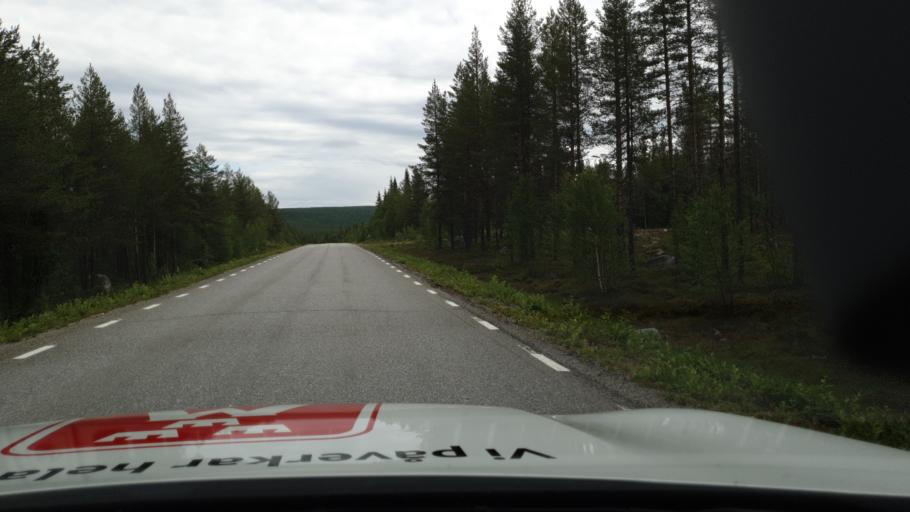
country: SE
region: Vaesterbotten
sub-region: Sorsele Kommun
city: Sorsele
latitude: 65.5218
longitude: 17.1251
